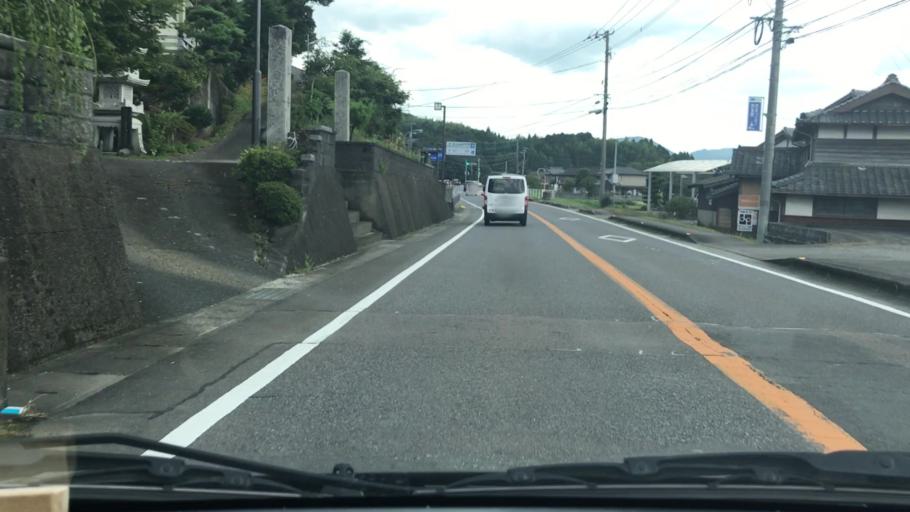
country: JP
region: Saga Prefecture
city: Takeocho-takeo
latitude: 33.2274
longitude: 130.0231
